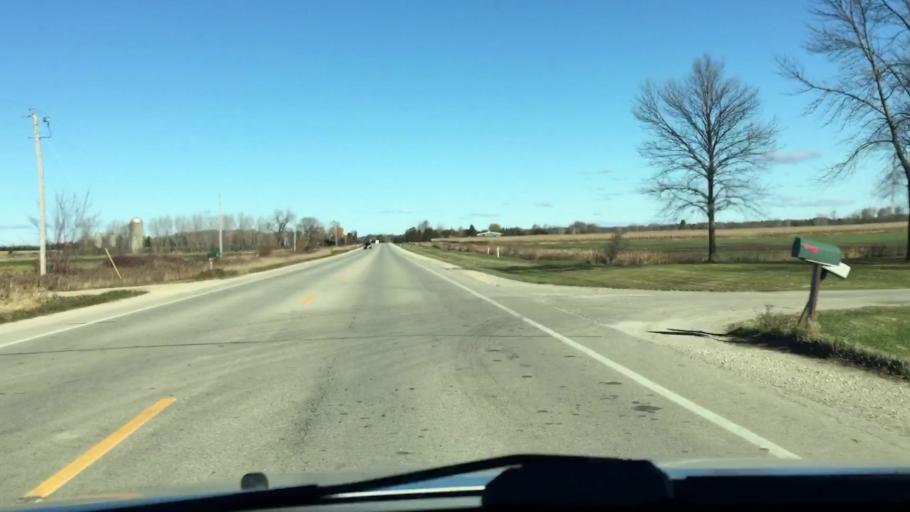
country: US
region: Wisconsin
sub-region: Brown County
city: Pulaski
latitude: 44.7347
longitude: -88.2474
